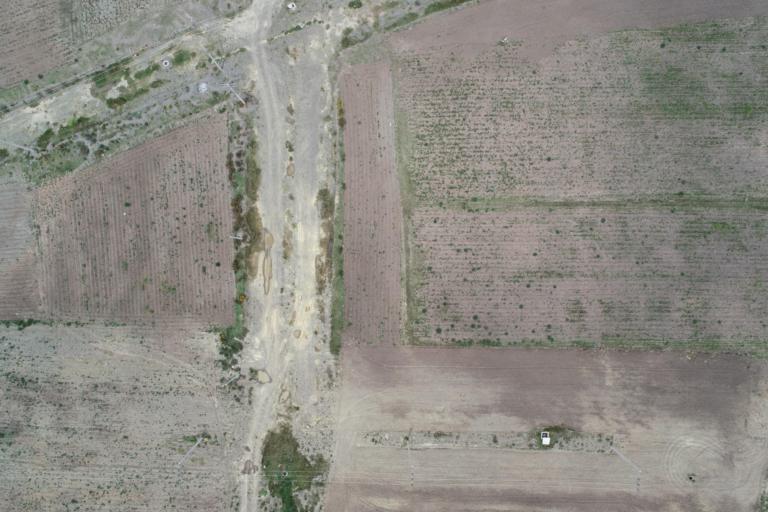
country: BO
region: La Paz
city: La Paz
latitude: -16.5147
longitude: -68.3032
